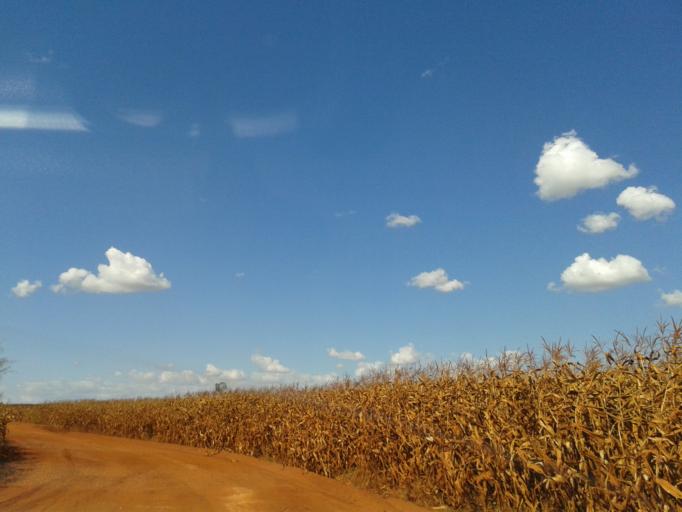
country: BR
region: Minas Gerais
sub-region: Capinopolis
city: Capinopolis
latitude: -18.5986
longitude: -49.5166
